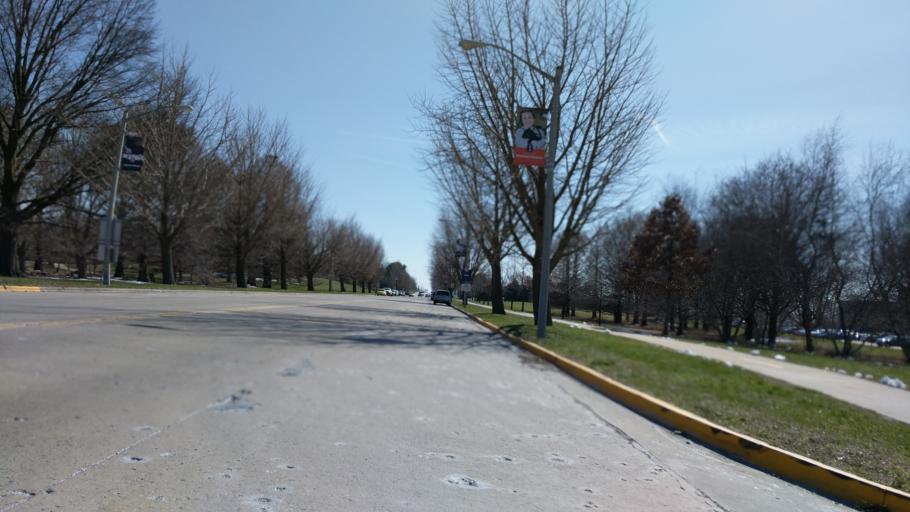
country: US
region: Illinois
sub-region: Champaign County
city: Urbana
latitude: 40.0944
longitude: -88.2192
